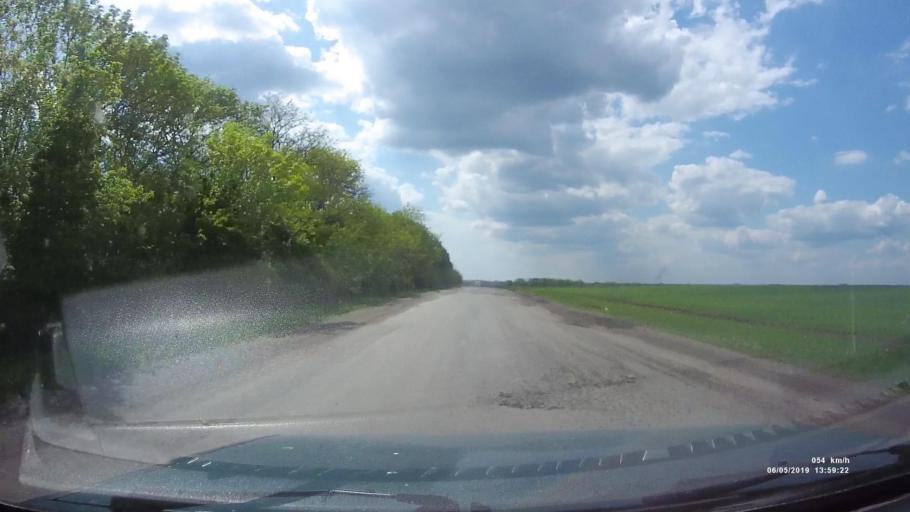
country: RU
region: Rostov
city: Shakhty
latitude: 47.6854
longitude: 40.4000
